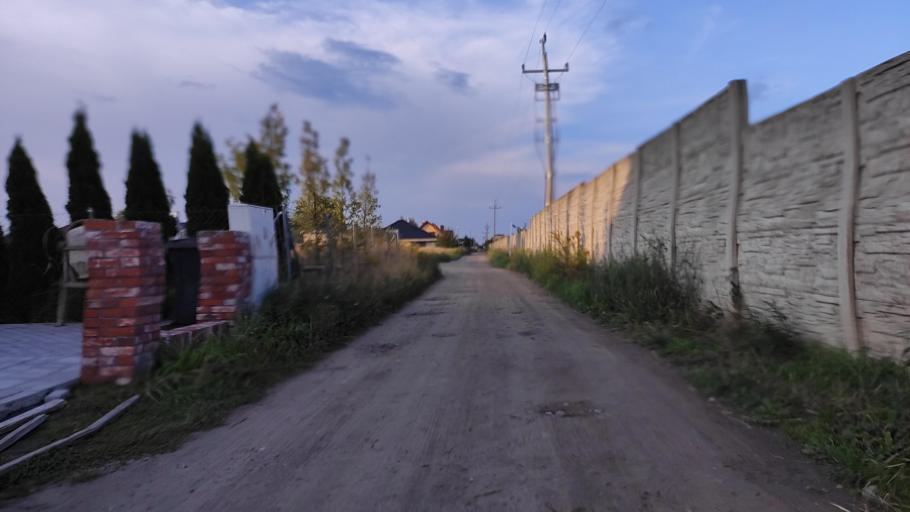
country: PL
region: Greater Poland Voivodeship
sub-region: Powiat poznanski
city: Kleszczewo
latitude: 52.3918
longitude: 17.1644
